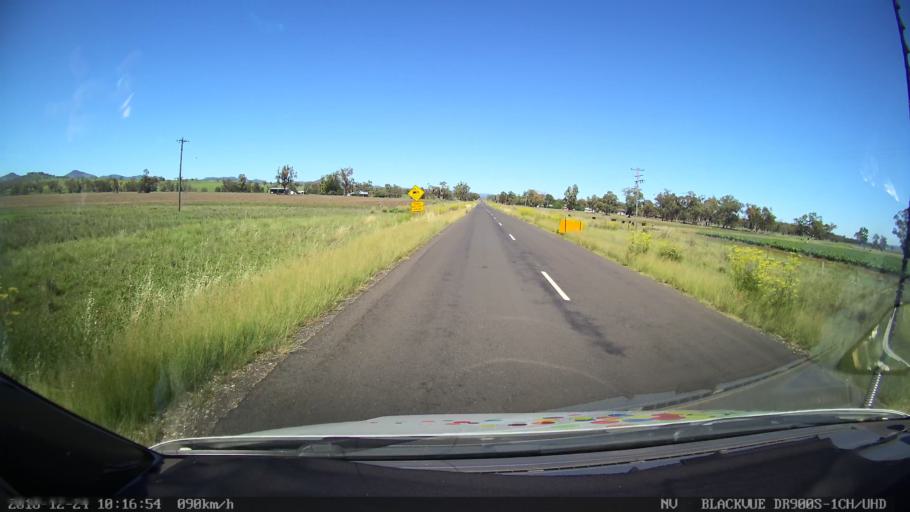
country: AU
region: New South Wales
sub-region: Liverpool Plains
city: Quirindi
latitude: -31.7180
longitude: 150.5994
